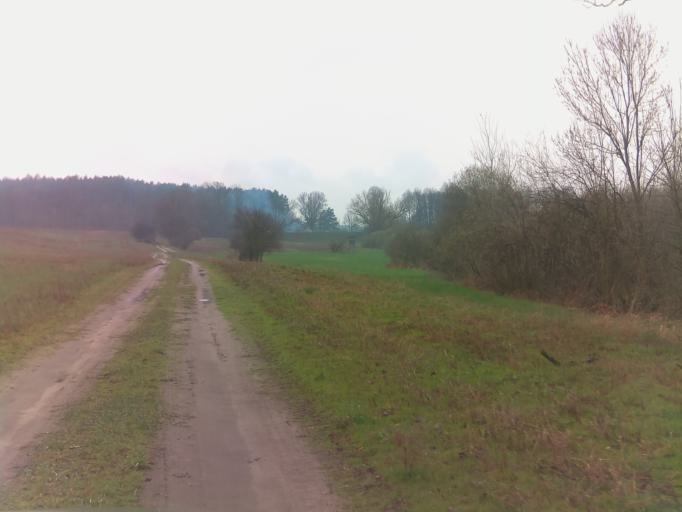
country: DE
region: Brandenburg
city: Lieberose
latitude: 52.0104
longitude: 14.2199
